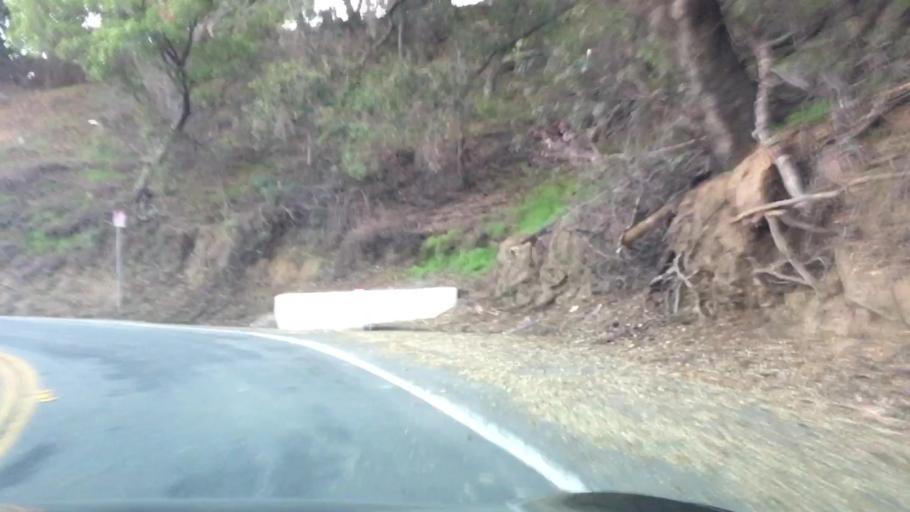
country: US
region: California
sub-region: Los Angeles County
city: Hacienda Heights
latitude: 33.9947
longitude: -117.9919
